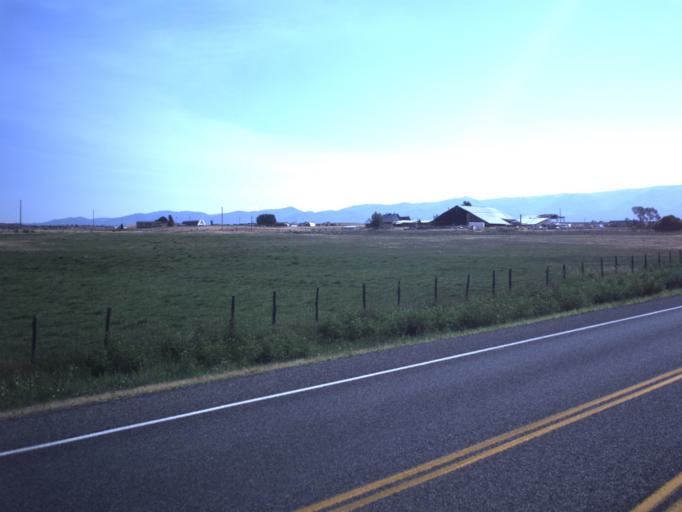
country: US
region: Utah
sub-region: Sanpete County
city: Moroni
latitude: 39.5249
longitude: -111.5675
